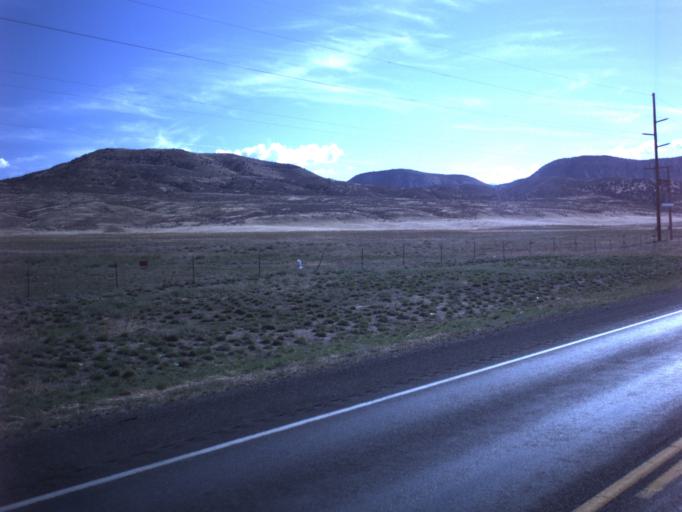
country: US
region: Utah
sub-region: Sanpete County
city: Gunnison
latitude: 39.2434
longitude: -111.8527
